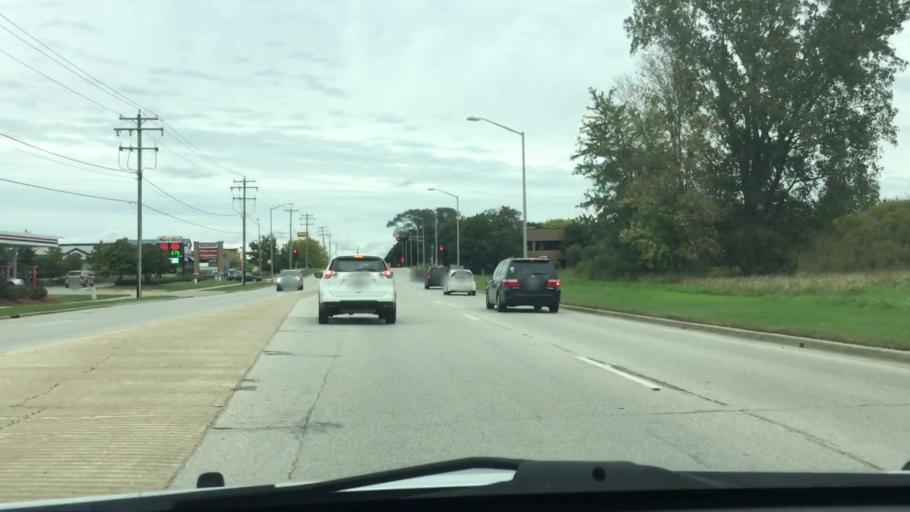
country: US
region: Wisconsin
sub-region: Waukesha County
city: Waukesha
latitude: 43.0384
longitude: -88.2558
